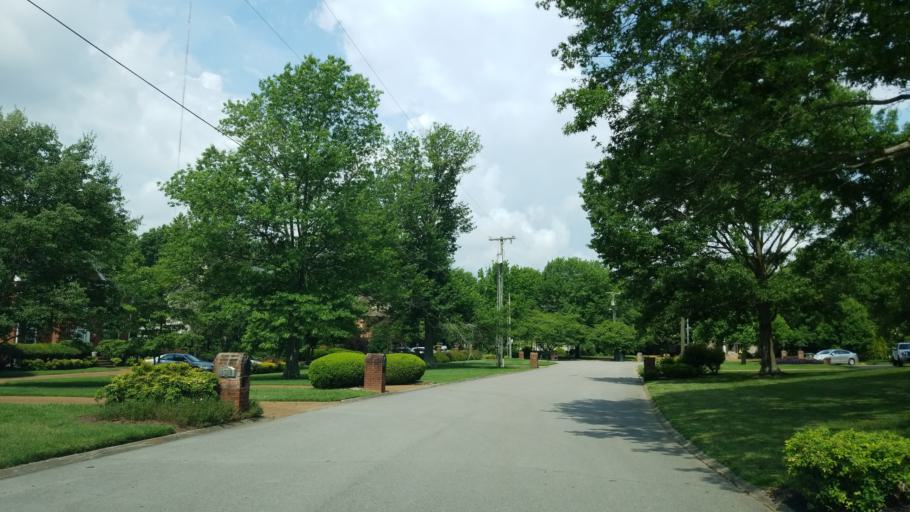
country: US
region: Tennessee
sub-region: Davidson County
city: Forest Hills
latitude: 36.0388
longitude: -86.8386
